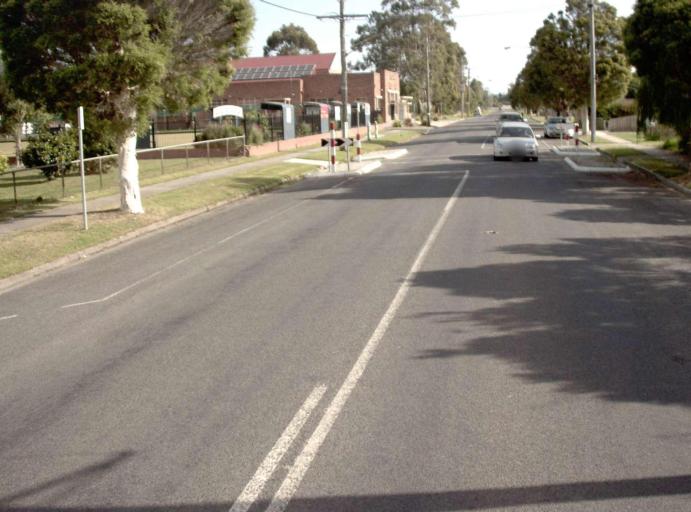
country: AU
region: Victoria
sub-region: Cardinia
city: Bunyip
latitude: -38.1126
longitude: 145.7677
